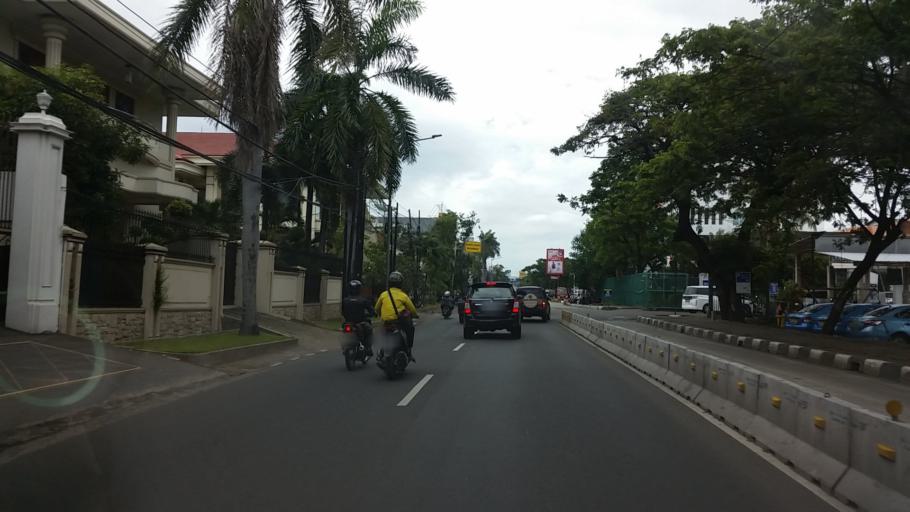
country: ID
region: Jakarta Raya
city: Jakarta
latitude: -6.1179
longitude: 106.7909
